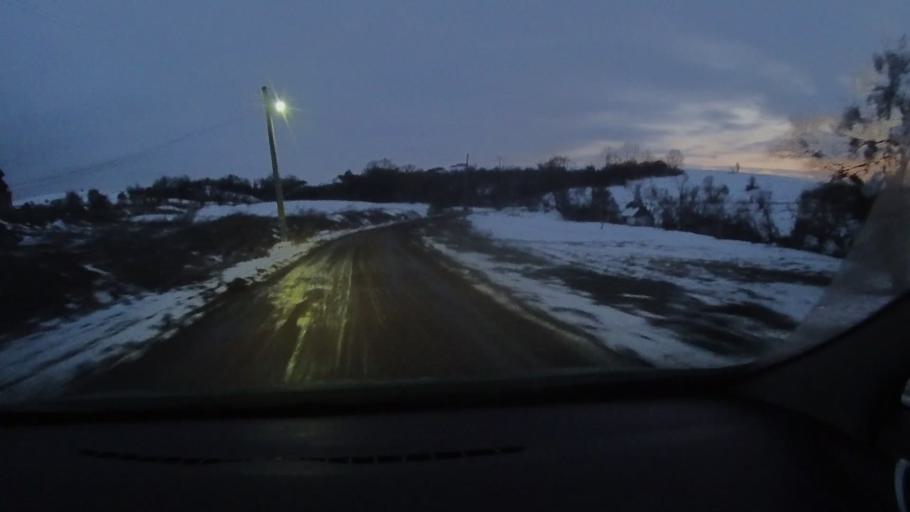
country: RO
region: Harghita
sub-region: Comuna Darjiu
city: Darjiu
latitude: 46.1688
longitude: 25.2272
